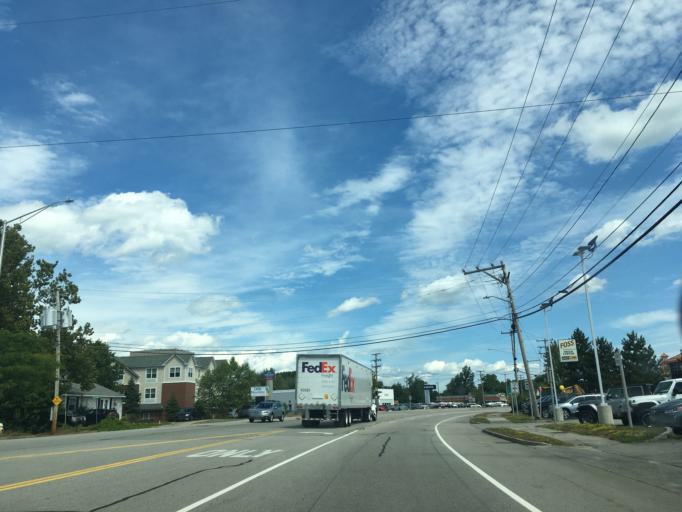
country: US
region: New Hampshire
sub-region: Rockingham County
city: Exeter
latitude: 42.9893
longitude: -70.9326
